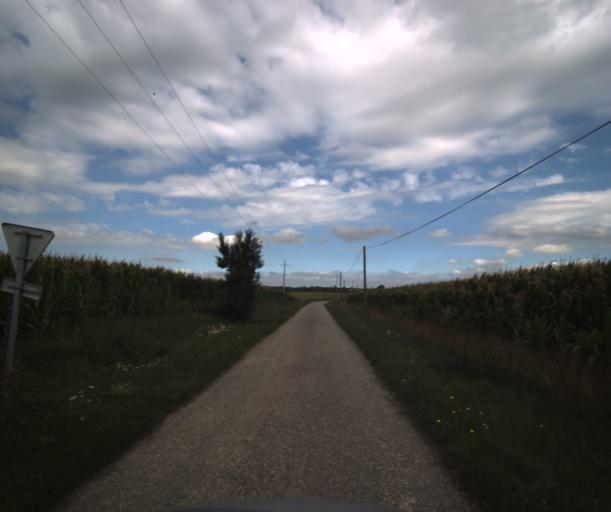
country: FR
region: Midi-Pyrenees
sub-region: Departement de la Haute-Garonne
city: Lacasse
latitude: 43.3948
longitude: 1.2398
